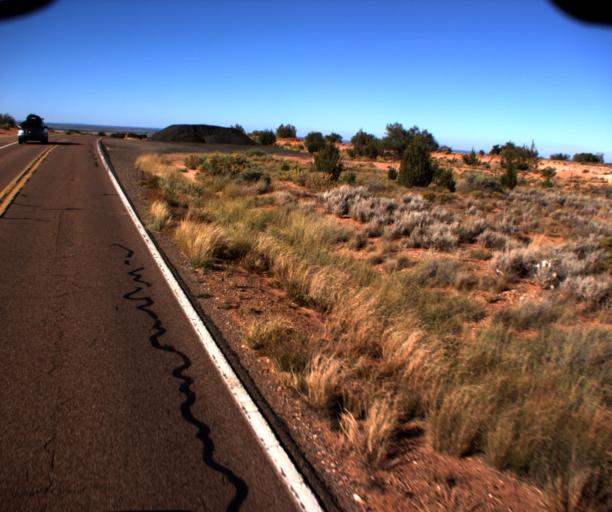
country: US
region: Arizona
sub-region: Navajo County
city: Snowflake
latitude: 34.6484
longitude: -110.3458
